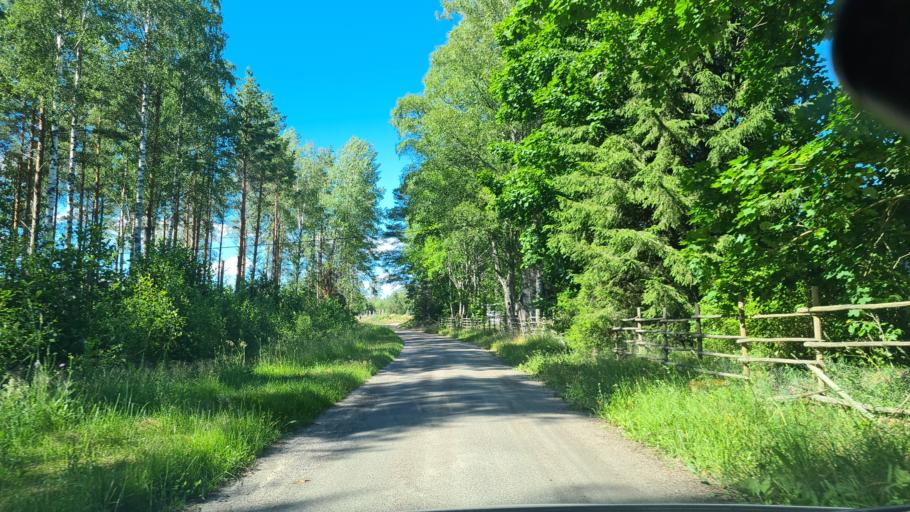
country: SE
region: OEstergoetland
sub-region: Norrkopings Kommun
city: Krokek
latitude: 58.6976
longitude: 16.4271
